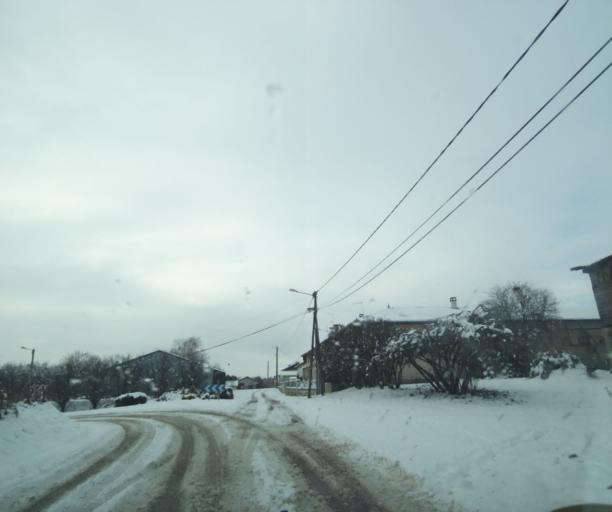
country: FR
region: Champagne-Ardenne
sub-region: Departement de la Haute-Marne
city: Montier-en-Der
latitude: 48.5197
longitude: 4.7007
